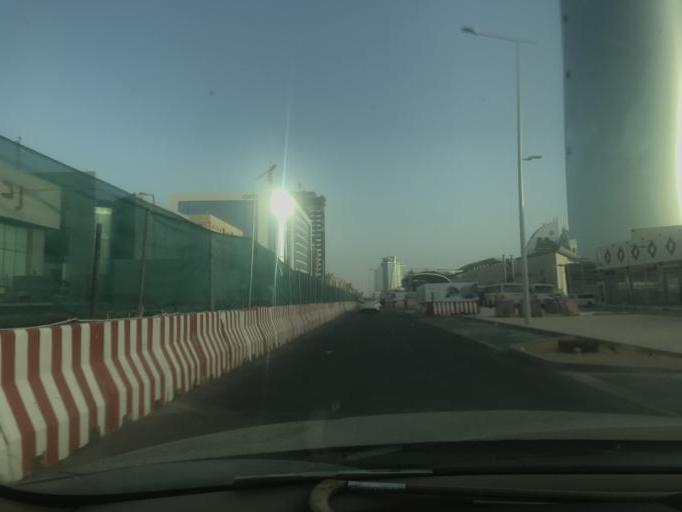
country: SA
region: Ar Riyad
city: Riyadh
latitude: 24.7156
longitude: 46.6741
